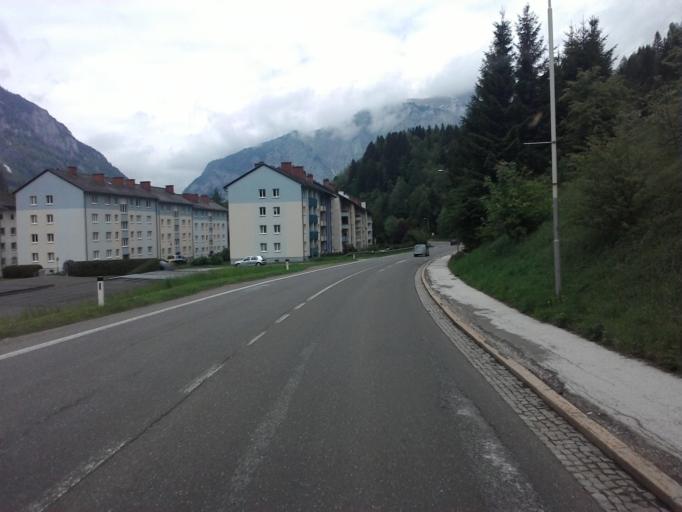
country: AT
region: Styria
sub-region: Politischer Bezirk Leoben
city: Eisenerz
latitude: 47.5488
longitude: 14.8787
